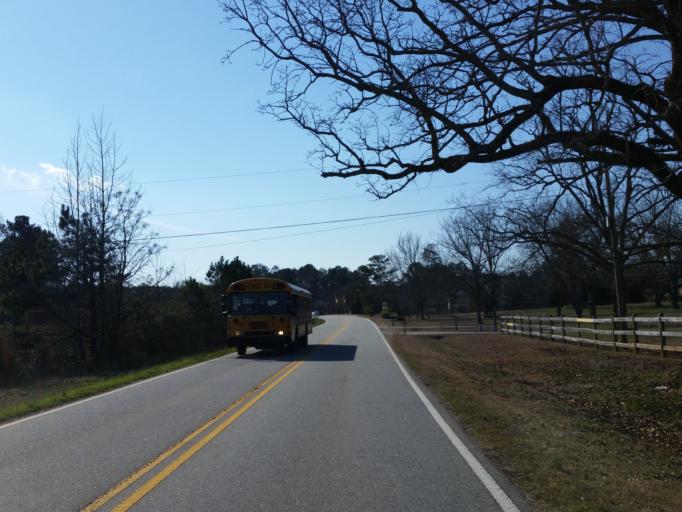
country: US
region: Georgia
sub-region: Henry County
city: Hampton
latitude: 33.4450
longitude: -84.2358
